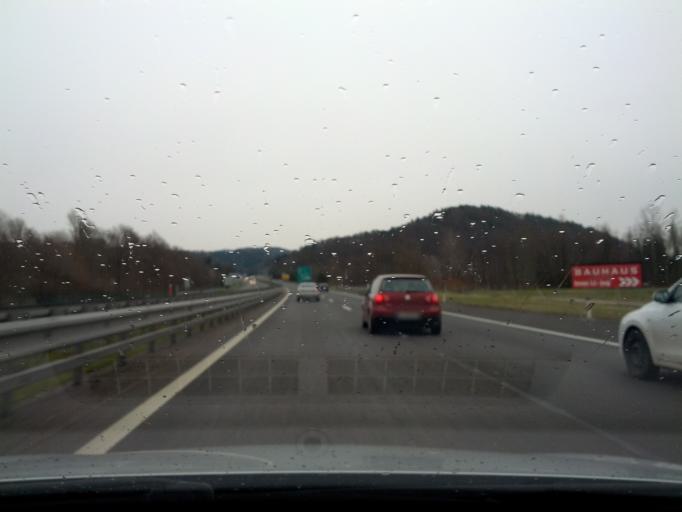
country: SI
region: Skofljica
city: Lavrica
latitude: 46.0152
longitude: 14.5336
